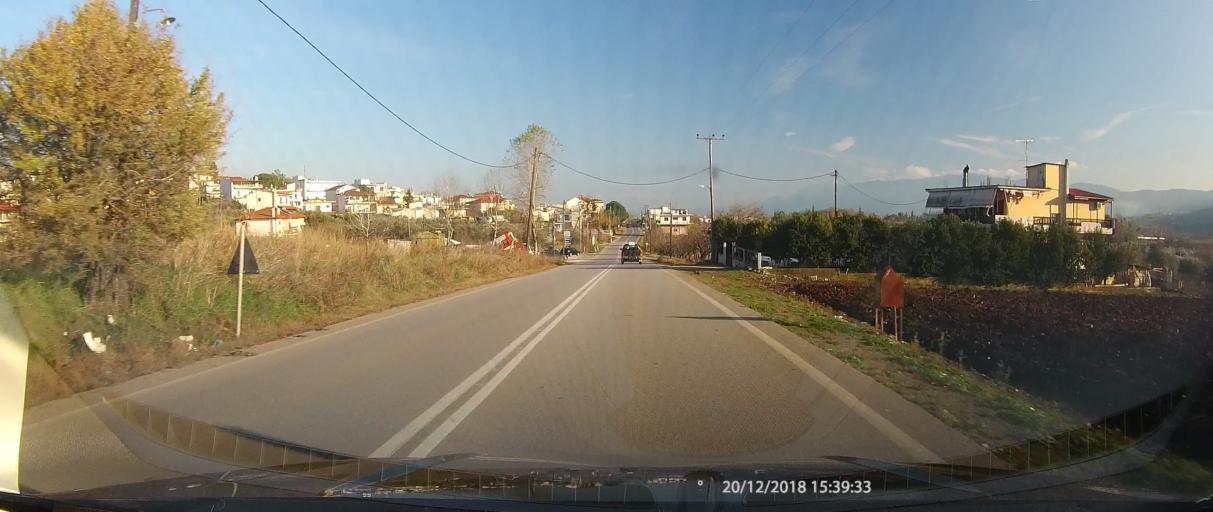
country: GR
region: Central Greece
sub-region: Nomos Fthiotidos
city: Stavros
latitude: 38.8956
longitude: 22.3664
